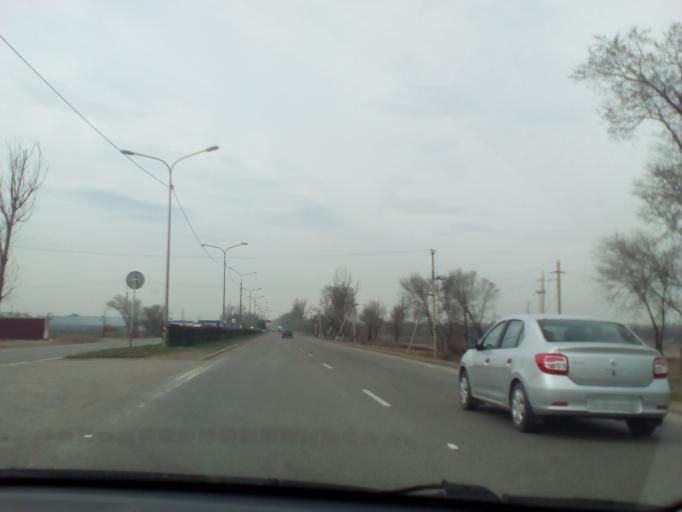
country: KZ
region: Almaty Oblysy
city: Burunday
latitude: 43.2211
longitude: 76.6270
